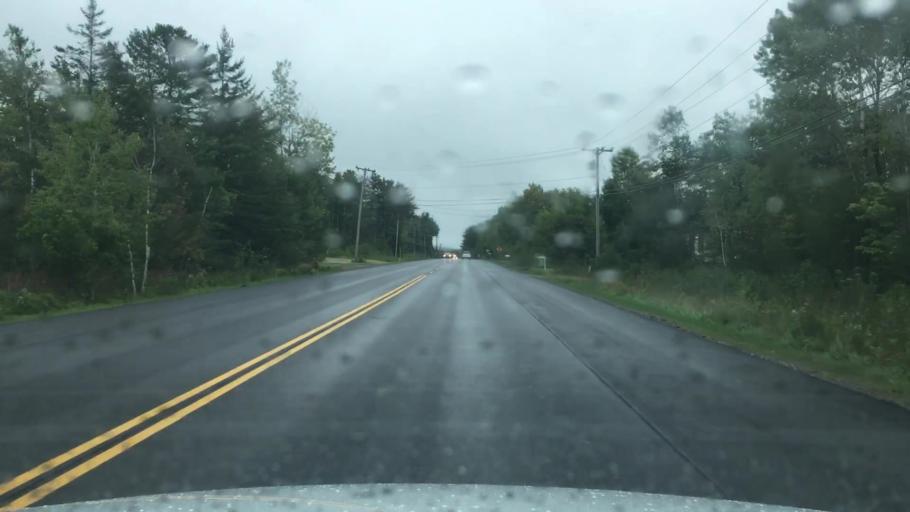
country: US
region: Maine
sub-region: Penobscot County
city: Hampden
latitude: 44.7585
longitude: -68.8450
